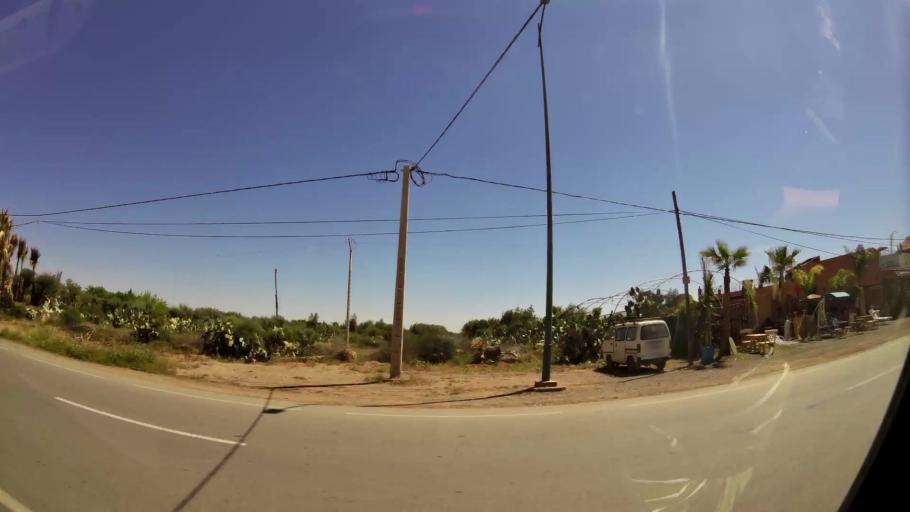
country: MA
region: Marrakech-Tensift-Al Haouz
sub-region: Marrakech
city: Marrakesh
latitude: 31.5584
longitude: -7.9772
